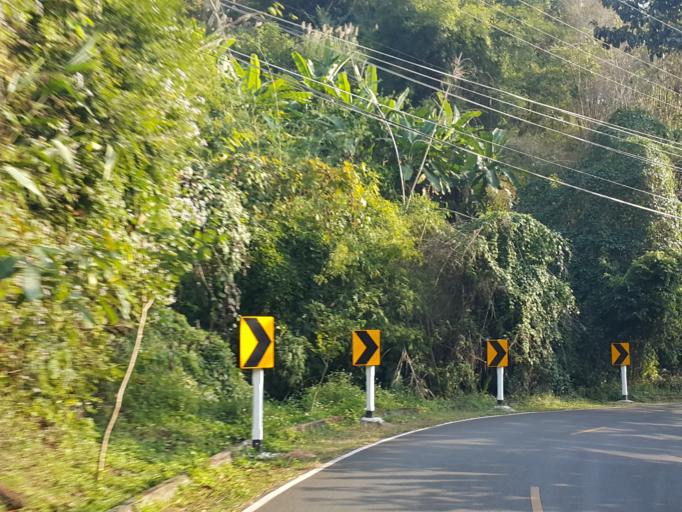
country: TH
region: Chiang Mai
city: Samoeng
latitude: 18.9044
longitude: 98.8306
